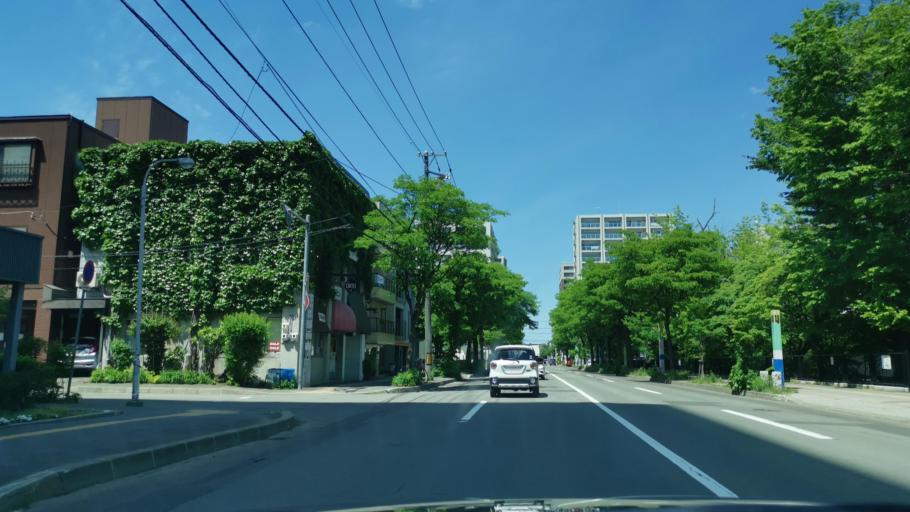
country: JP
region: Hokkaido
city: Sapporo
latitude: 43.0595
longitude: 141.3297
